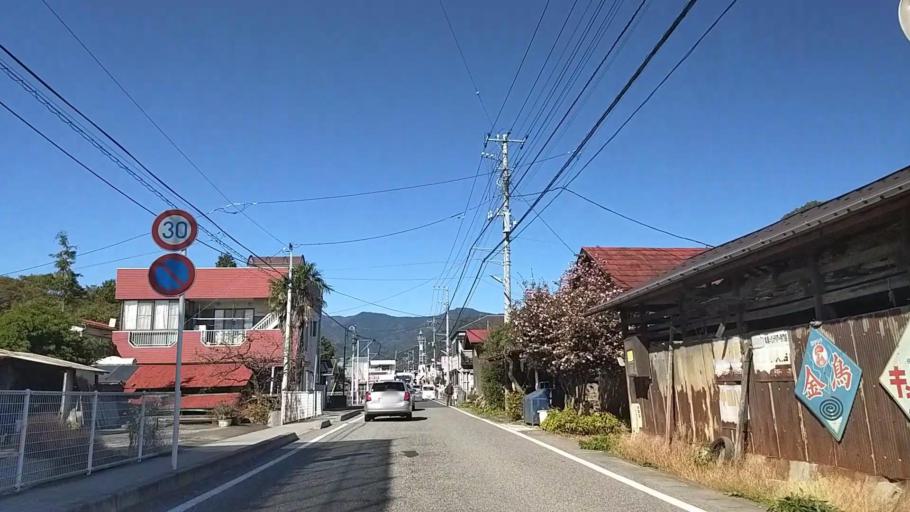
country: JP
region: Yamanashi
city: Uenohara
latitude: 35.6364
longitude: 139.1068
